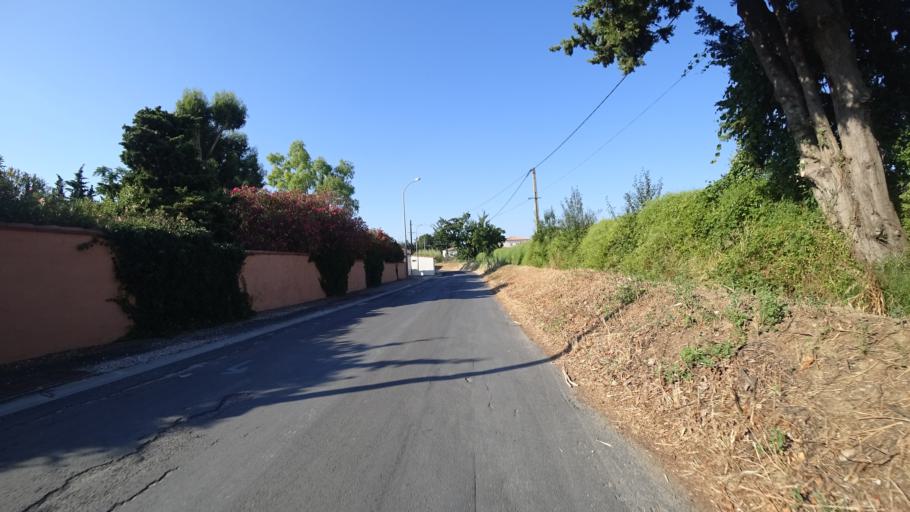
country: FR
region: Languedoc-Roussillon
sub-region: Departement des Pyrenees-Orientales
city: Cabestany
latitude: 42.6931
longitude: 2.9695
